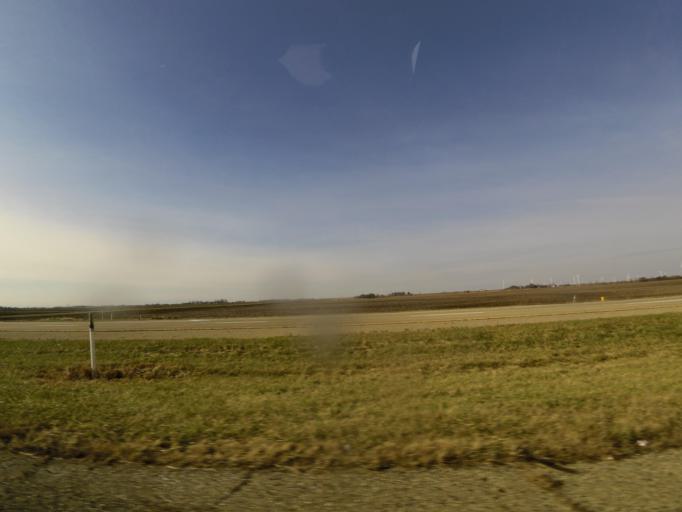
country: US
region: Illinois
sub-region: Macon County
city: Forsyth
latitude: 39.9502
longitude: -88.9554
